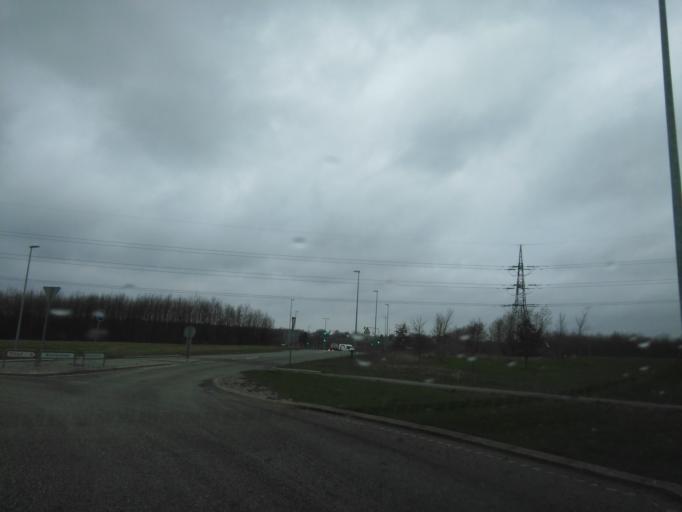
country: DK
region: Central Jutland
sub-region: Arhus Kommune
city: Stavtrup
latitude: 56.1649
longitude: 10.0952
